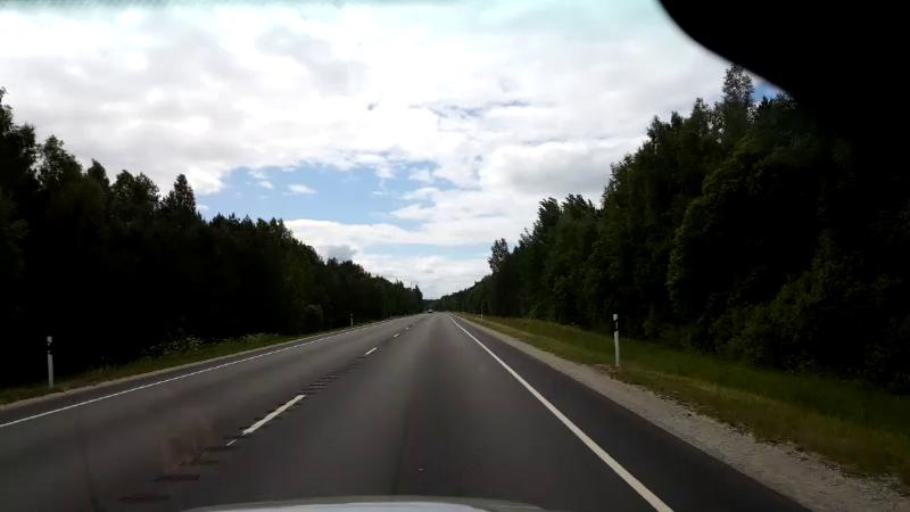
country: LV
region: Salacgrivas
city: Ainazi
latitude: 58.0946
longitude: 24.5079
